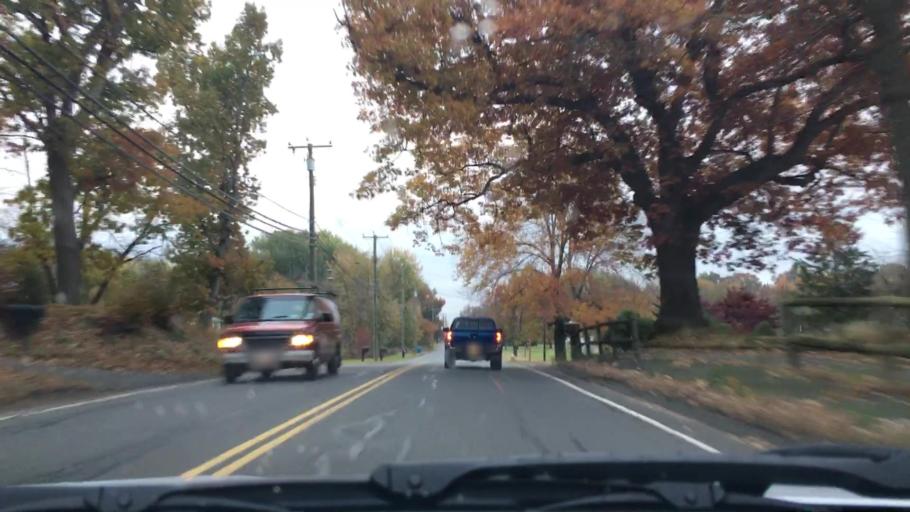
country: US
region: Massachusetts
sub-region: Hampden County
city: Agawam
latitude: 42.0662
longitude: -72.6880
